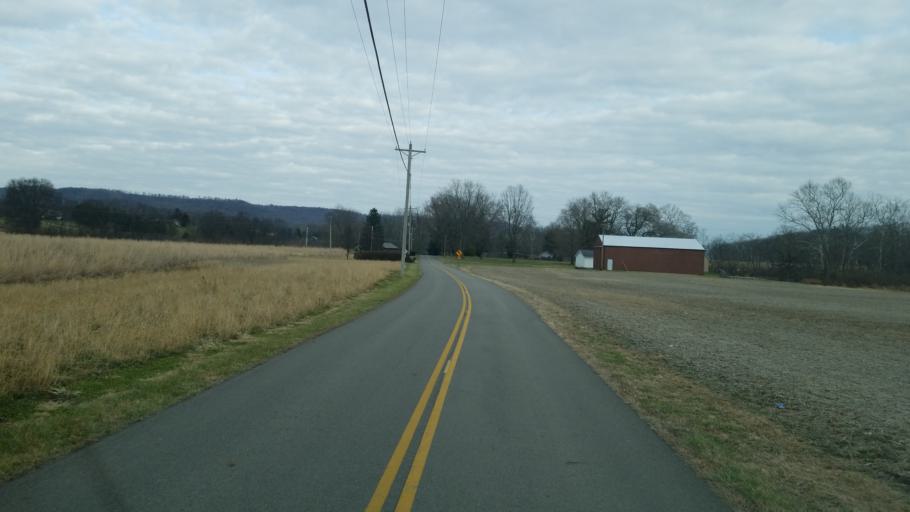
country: US
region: Ohio
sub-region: Highland County
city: Greenfield
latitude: 39.2274
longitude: -83.2977
